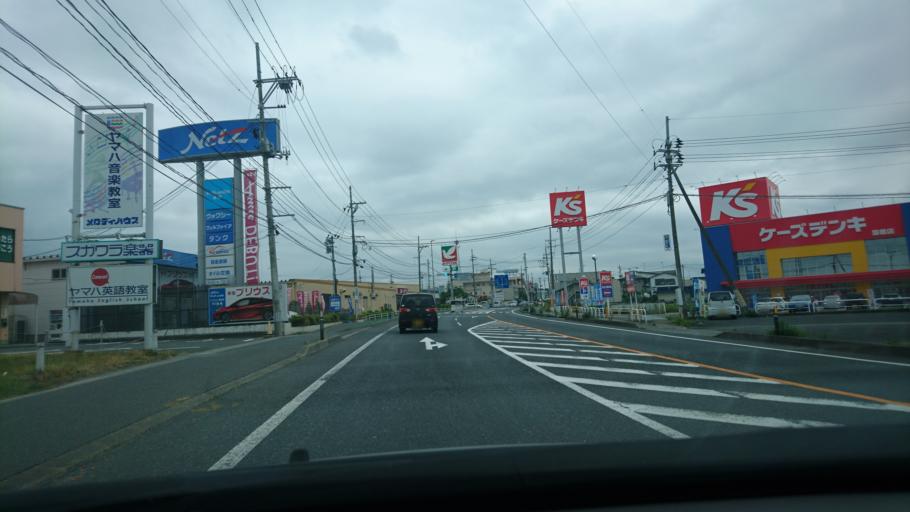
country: JP
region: Miyagi
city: Furukawa
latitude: 38.7373
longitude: 141.0221
